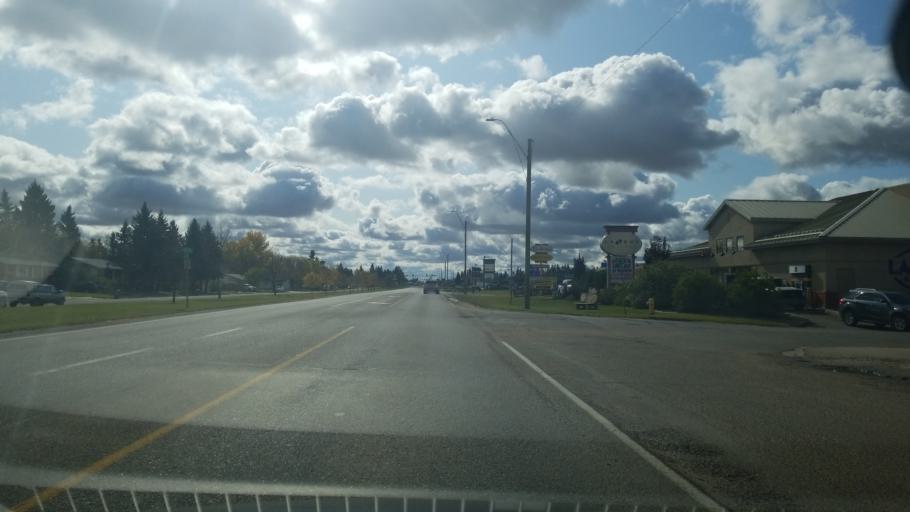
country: CA
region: Saskatchewan
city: Lloydminster
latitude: 53.2745
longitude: -110.0057
